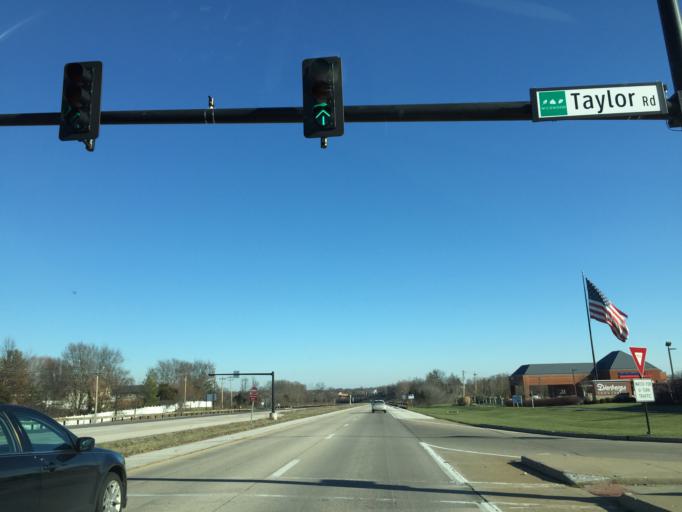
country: US
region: Missouri
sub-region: Saint Louis County
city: Wildwood
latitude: 38.5825
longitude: -90.6275
